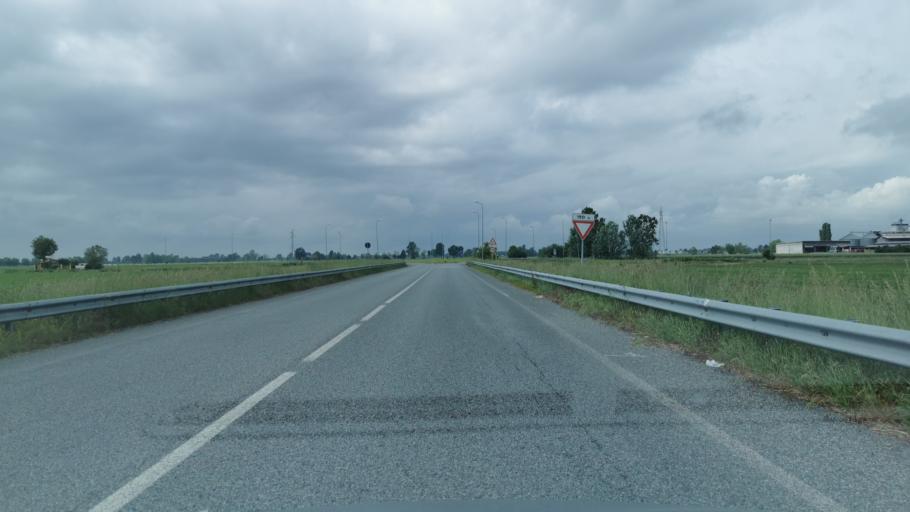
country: IT
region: Piedmont
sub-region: Provincia di Cuneo
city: Racconigi
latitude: 44.7650
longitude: 7.6981
